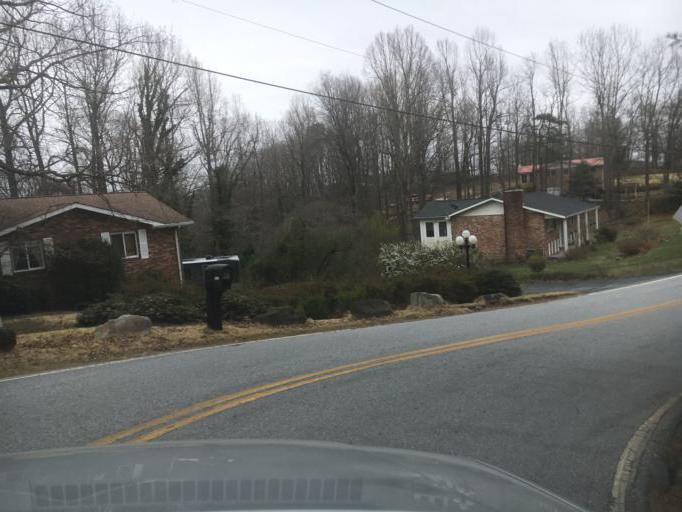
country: US
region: North Carolina
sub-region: Henderson County
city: East Flat Rock
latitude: 35.2543
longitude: -82.4140
